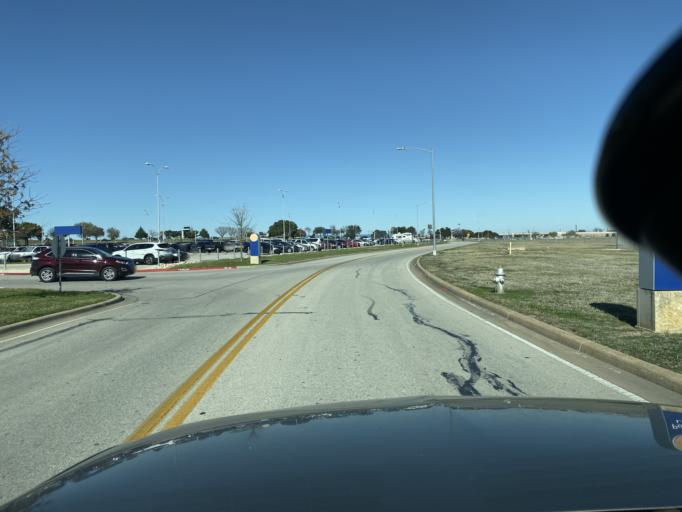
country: US
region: Texas
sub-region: Travis County
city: Hornsby Bend
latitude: 30.2076
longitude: -97.6610
